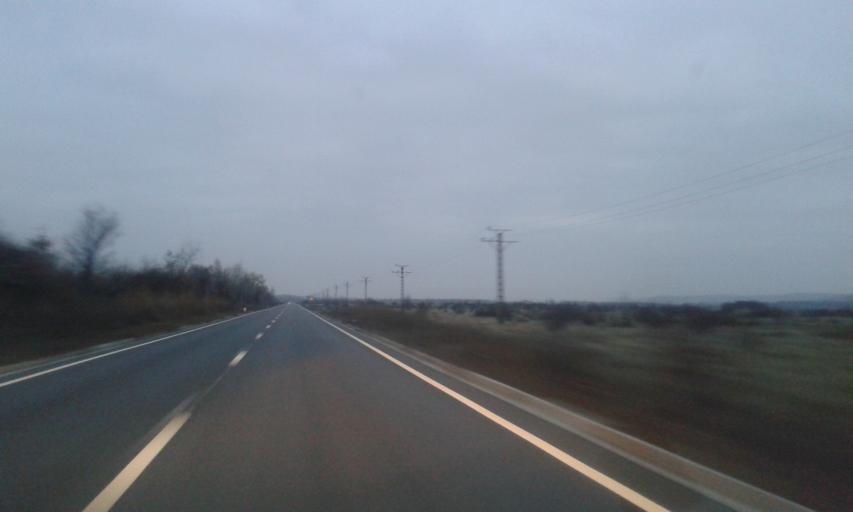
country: RO
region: Gorj
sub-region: Comuna Bumbesti-Jiu
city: Bumbesti-Jiu
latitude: 45.1517
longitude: 23.3728
